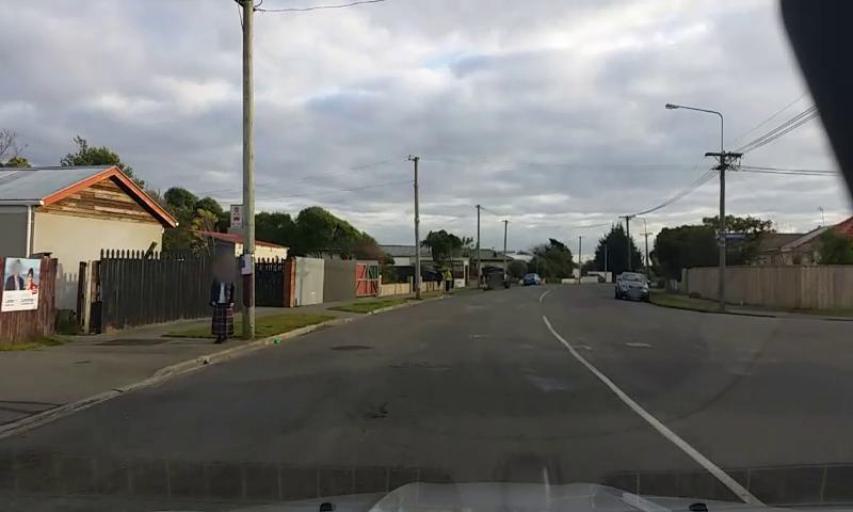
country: NZ
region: Canterbury
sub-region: Christchurch City
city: Christchurch
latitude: -43.5167
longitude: 172.7296
